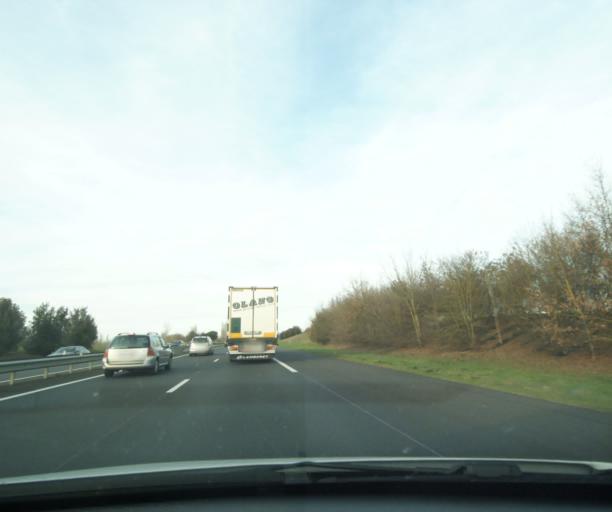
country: FR
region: Midi-Pyrenees
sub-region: Departement de la Haute-Garonne
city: Saubens
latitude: 43.4936
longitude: 1.3339
